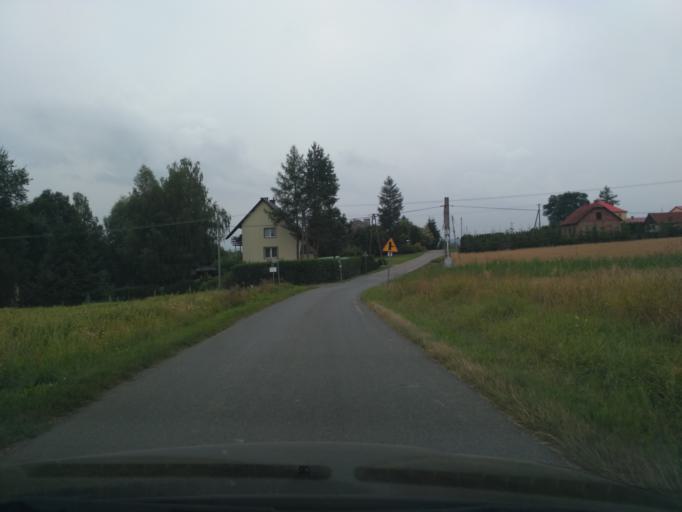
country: PL
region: Subcarpathian Voivodeship
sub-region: Powiat strzyzowski
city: Wysoka Strzyzowska
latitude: 49.8619
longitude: 21.7140
